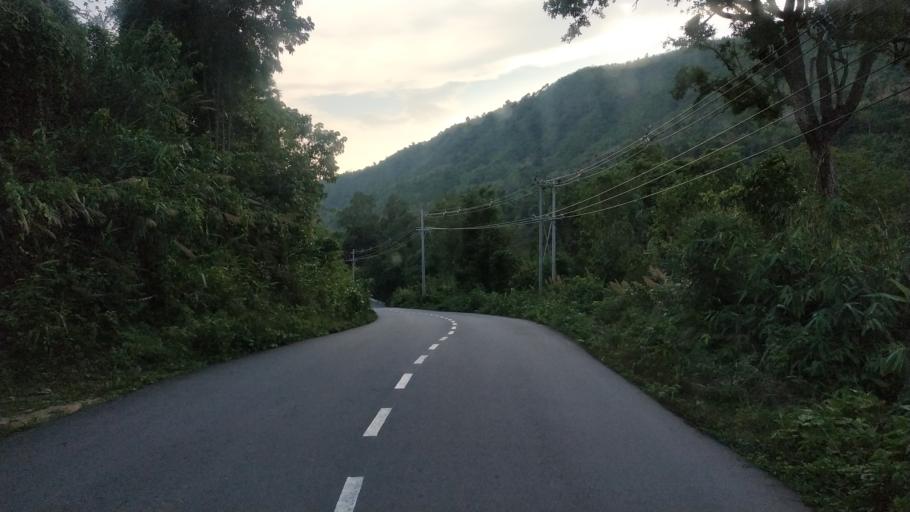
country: MM
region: Mon
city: Kyaikto
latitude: 17.4271
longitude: 97.0859
